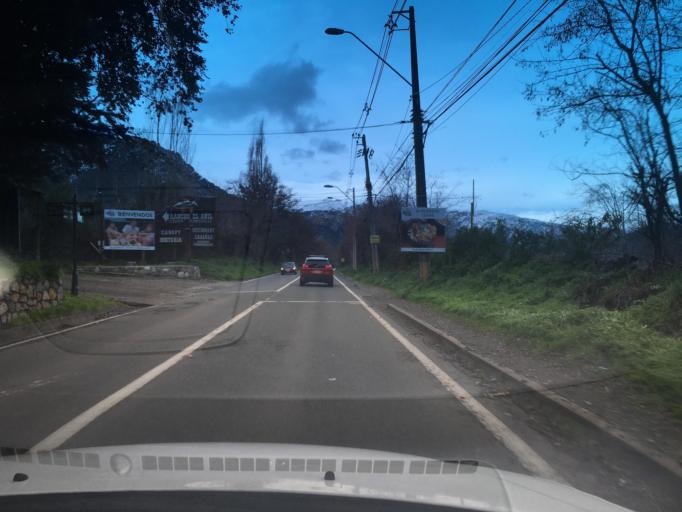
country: CL
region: Santiago Metropolitan
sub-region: Provincia de Cordillera
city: Puente Alto
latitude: -33.5790
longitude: -70.4153
